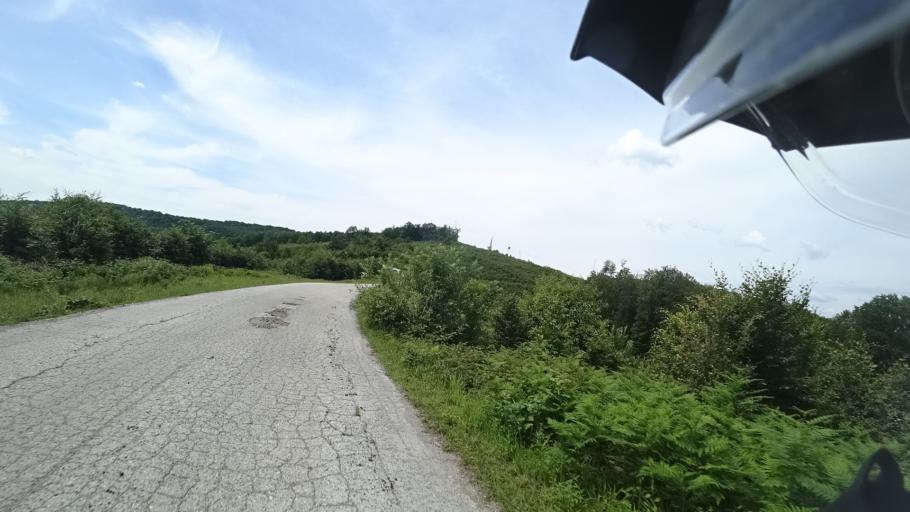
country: HR
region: Sisacko-Moslavacka
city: Gvozd
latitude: 45.3066
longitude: 15.8003
